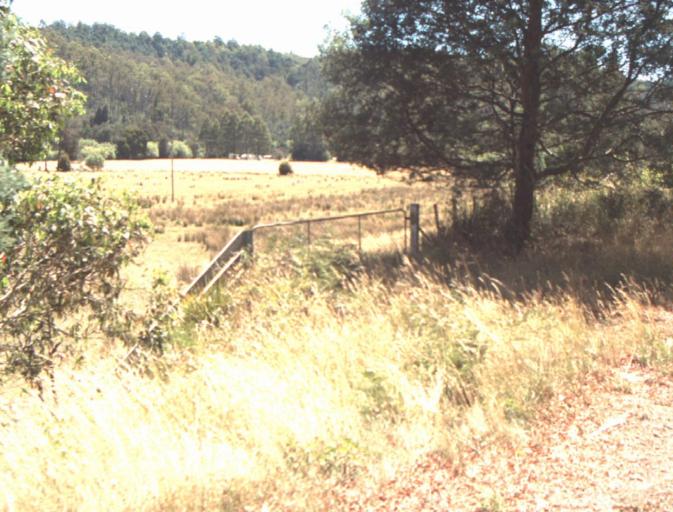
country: AU
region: Tasmania
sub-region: Dorset
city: Scottsdale
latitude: -41.3162
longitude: 147.3667
